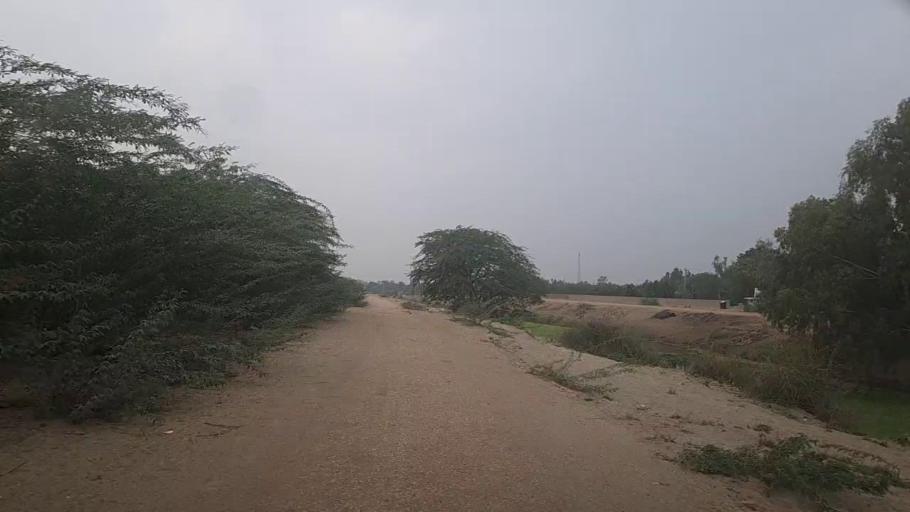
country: PK
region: Sindh
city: Gambat
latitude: 27.3599
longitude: 68.5701
